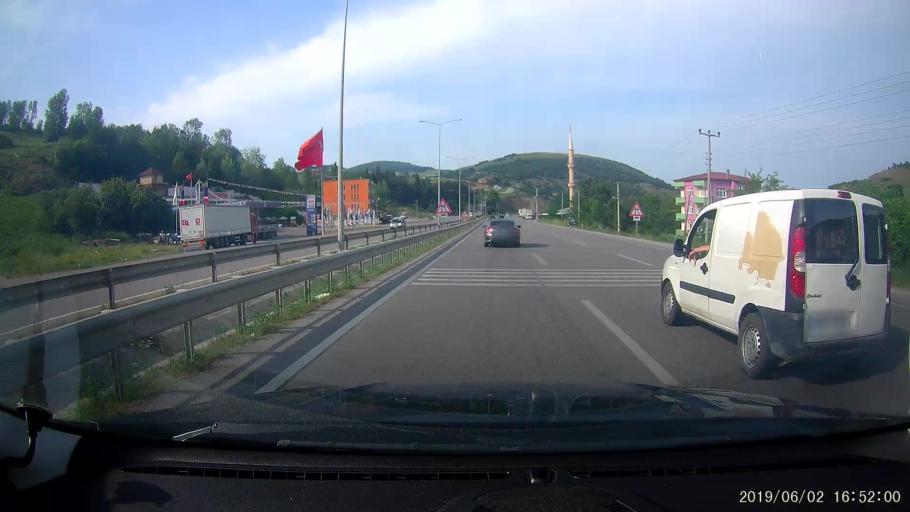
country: TR
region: Samsun
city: Samsun
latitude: 41.2816
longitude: 36.1911
